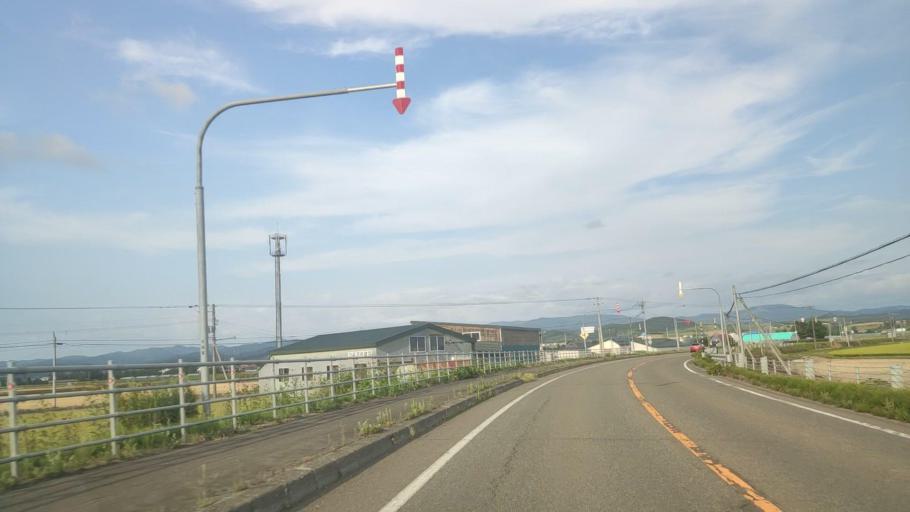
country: JP
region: Hokkaido
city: Iwamizawa
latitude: 43.0281
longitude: 141.8142
